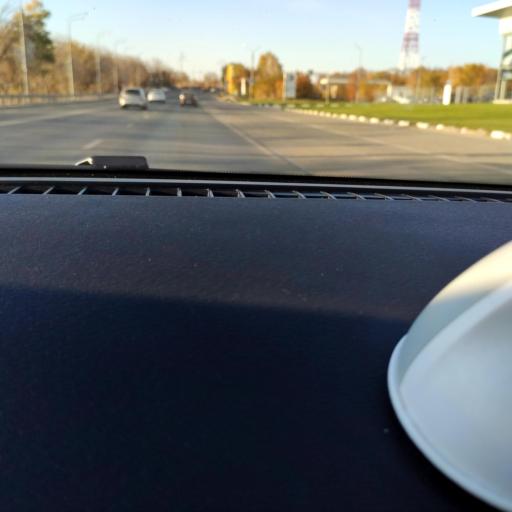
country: RU
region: Samara
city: Samara
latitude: 53.2870
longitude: 50.2257
